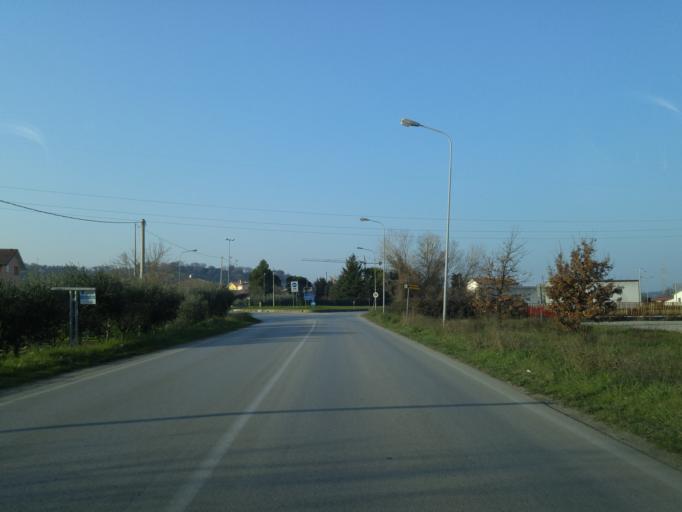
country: IT
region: The Marches
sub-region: Provincia di Pesaro e Urbino
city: Rosciano
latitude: 43.8152
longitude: 13.0001
